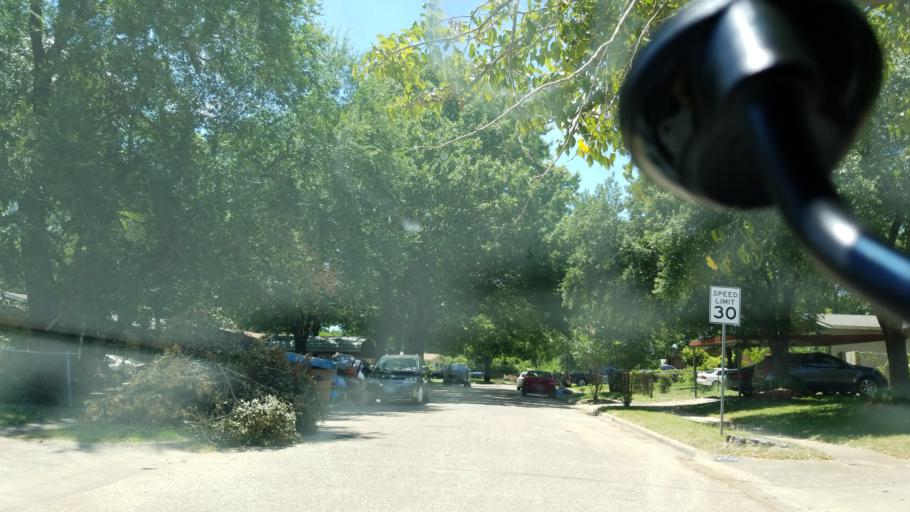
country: US
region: Texas
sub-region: Dallas County
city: Cockrell Hill
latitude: 32.6919
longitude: -96.8149
